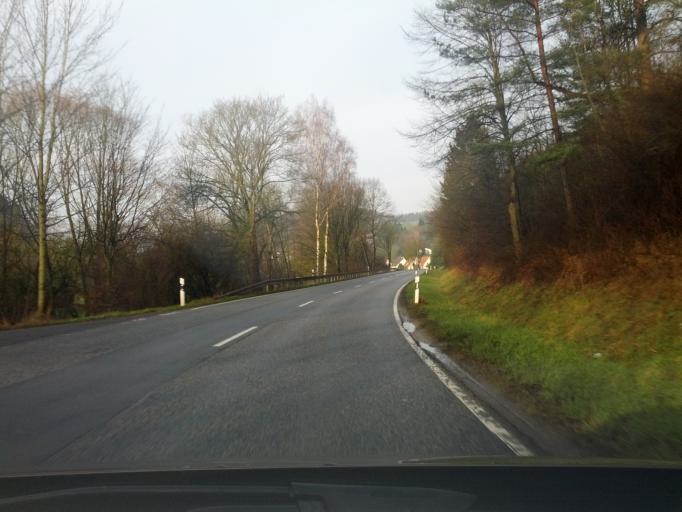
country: DE
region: Hesse
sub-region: Regierungsbezirk Kassel
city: Eschwege
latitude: 51.1155
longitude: 10.0383
